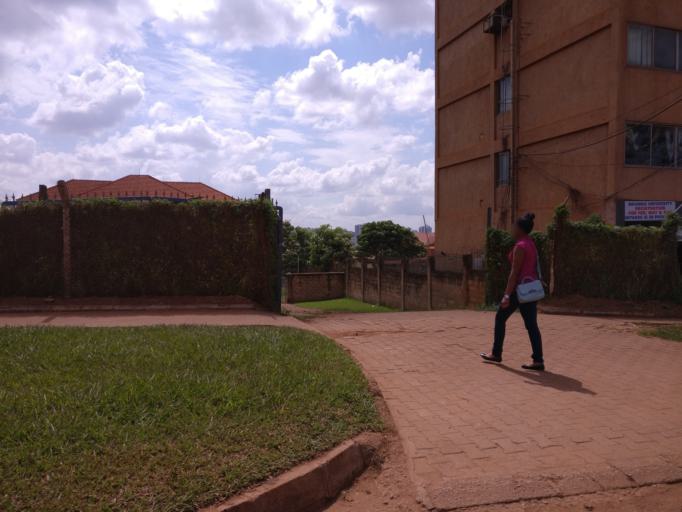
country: UG
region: Central Region
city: Kampala Central Division
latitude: 0.3063
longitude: 32.5620
